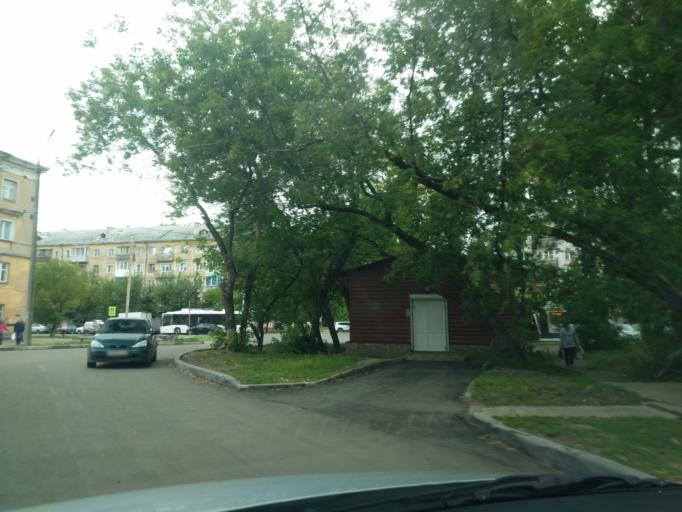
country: RU
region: Kirov
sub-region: Kirovo-Chepetskiy Rayon
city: Kirov
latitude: 58.6371
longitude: 49.6195
